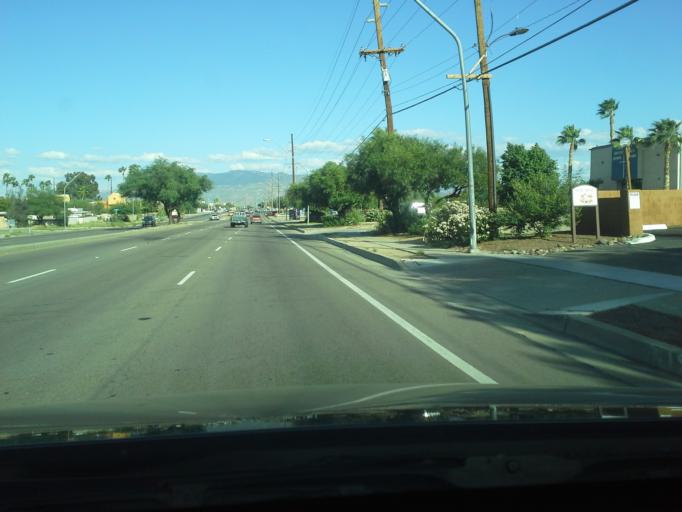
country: US
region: Arizona
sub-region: Pima County
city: Tucson
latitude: 32.1918
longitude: -110.8465
